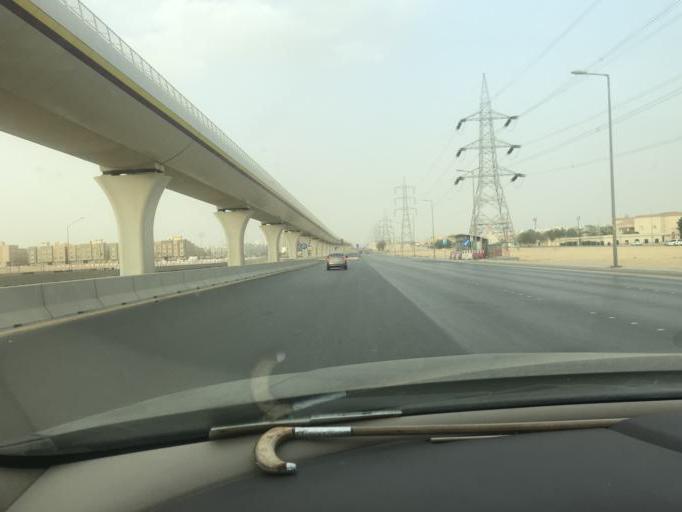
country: SA
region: Ar Riyad
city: Riyadh
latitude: 24.7889
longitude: 46.6666
